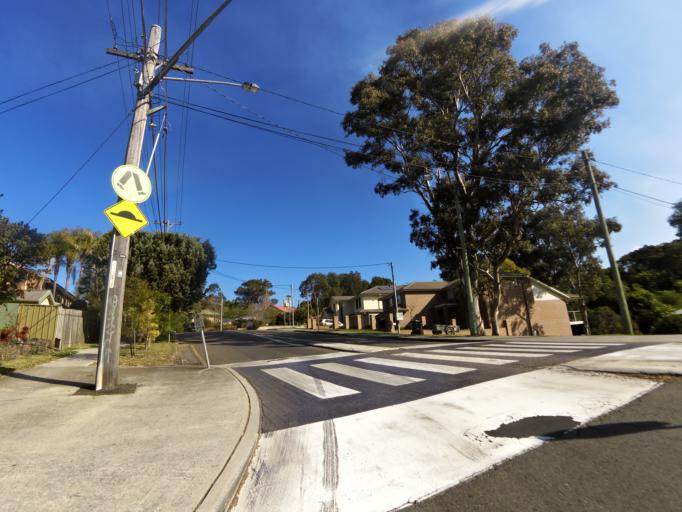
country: AU
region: New South Wales
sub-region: Sutherland Shire
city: Como
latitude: -34.0024
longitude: 151.0684
